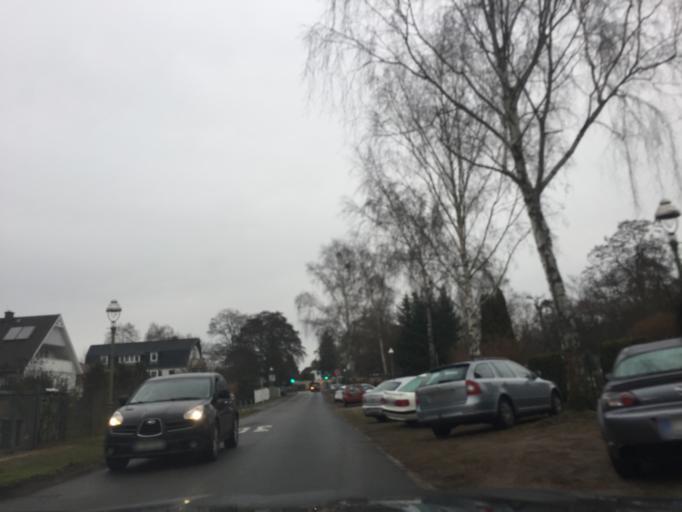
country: DE
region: Berlin
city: Wilhelmstadt
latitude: 52.5096
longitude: 13.1782
